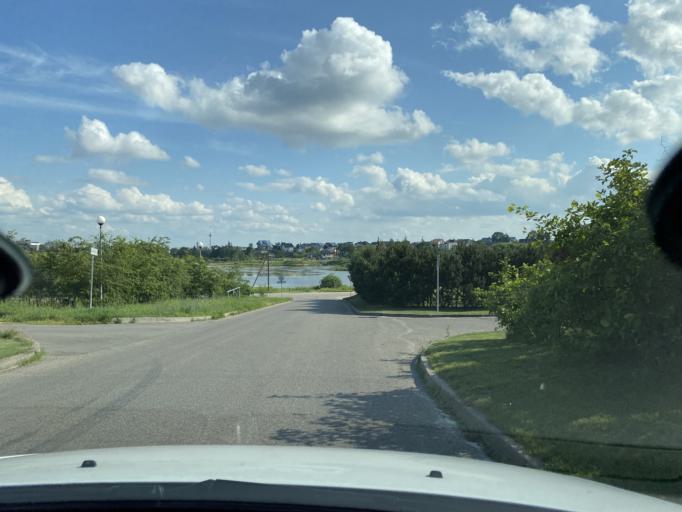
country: LT
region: Vilnius County
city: Pasilaiciai
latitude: 54.7366
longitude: 25.1981
